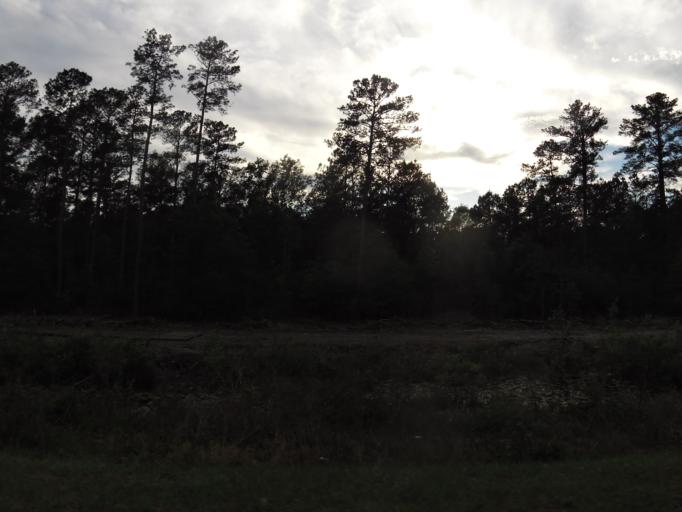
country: US
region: South Carolina
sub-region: Jasper County
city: Hardeeville
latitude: 32.4001
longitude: -81.0994
